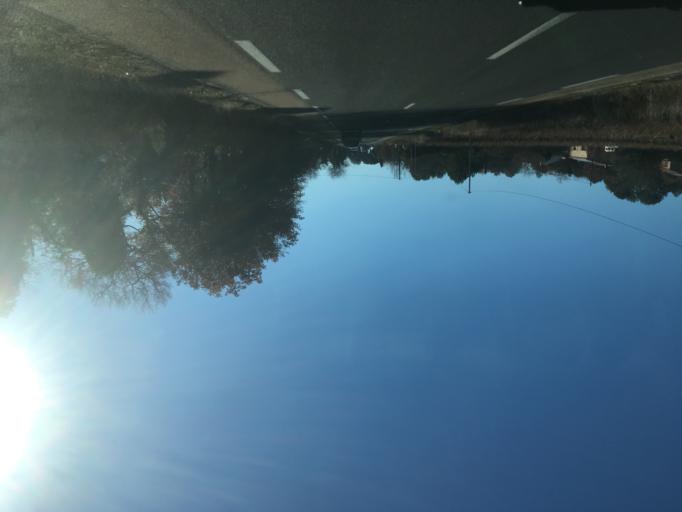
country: FR
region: Provence-Alpes-Cote d'Azur
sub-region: Departement du Var
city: Flayosc
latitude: 43.5320
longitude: 6.4132
